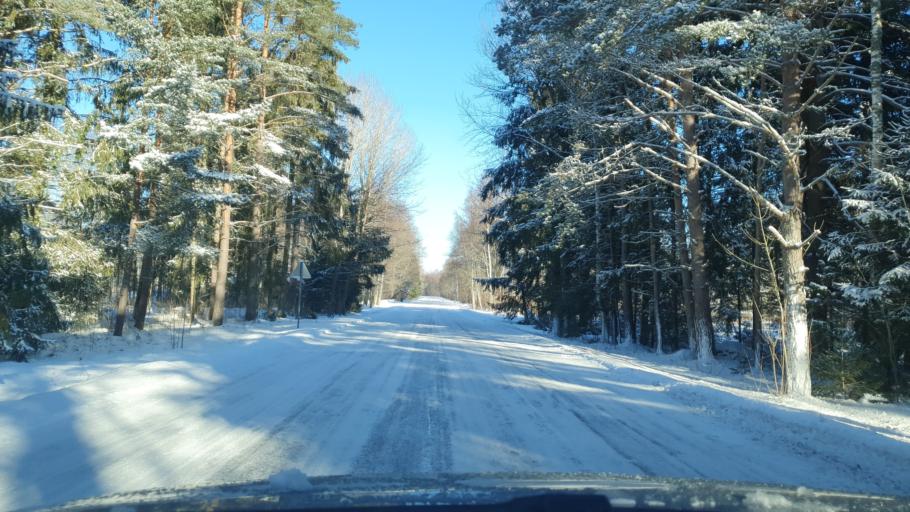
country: EE
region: Harju
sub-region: Kuusalu vald
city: Kuusalu
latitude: 59.5640
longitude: 25.5349
